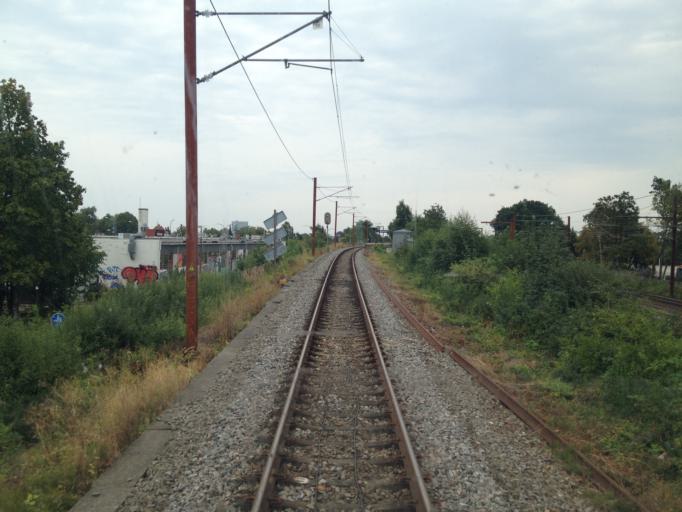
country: DK
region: Capital Region
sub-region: Rodovre Kommune
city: Rodovre
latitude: 55.6649
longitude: 12.4563
